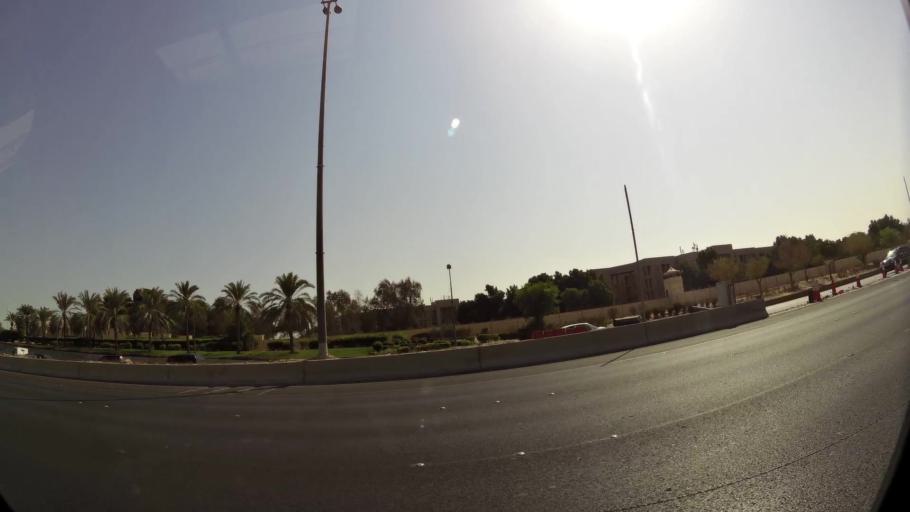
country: KW
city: Bayan
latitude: 29.3093
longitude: 48.0347
